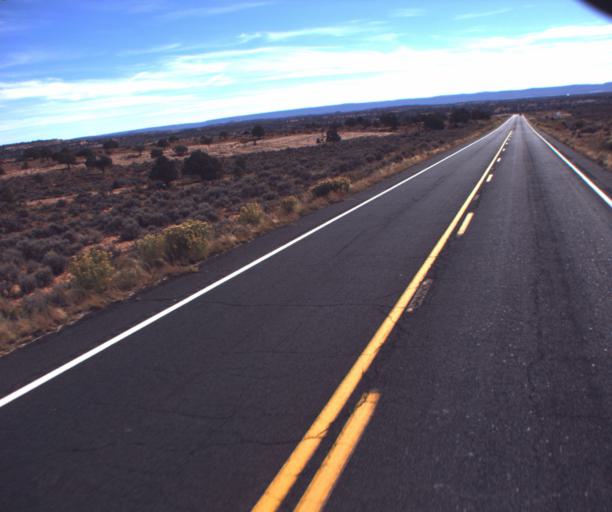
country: US
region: Arizona
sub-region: Coconino County
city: Kaibito
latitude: 36.5651
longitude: -110.7572
